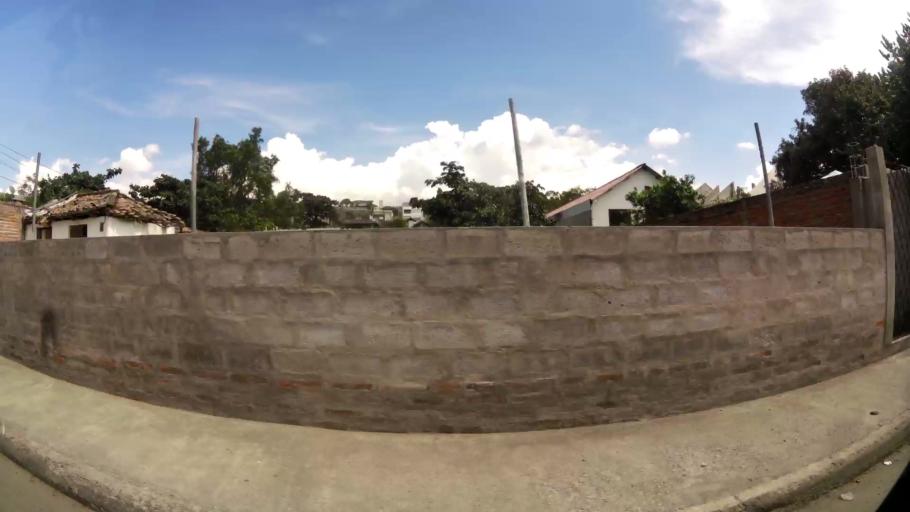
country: EC
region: Pichincha
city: Quito
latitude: -0.2164
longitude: -78.4311
